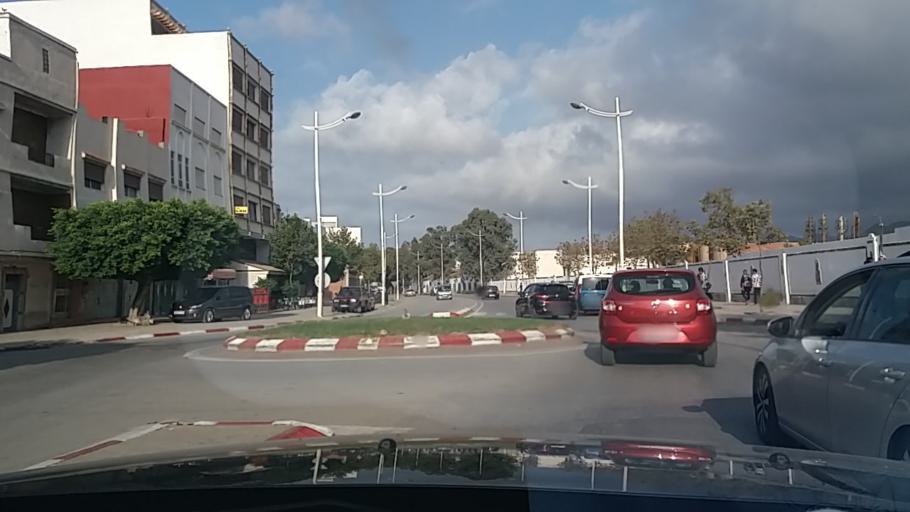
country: MA
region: Tanger-Tetouan
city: Tetouan
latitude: 35.5649
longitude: -5.3465
